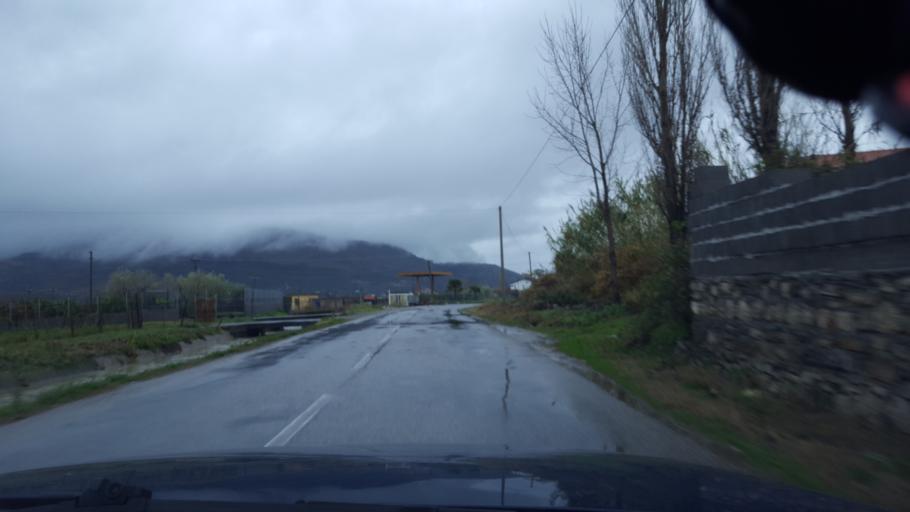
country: AL
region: Shkoder
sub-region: Rrethi i Shkodres
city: Berdica e Madhe
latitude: 42.0109
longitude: 19.4806
